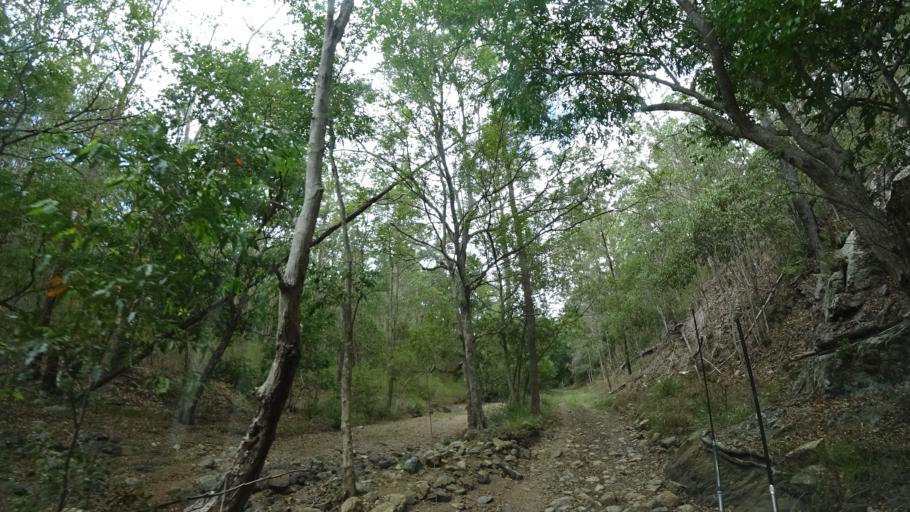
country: AU
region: Queensland
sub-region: Moreton Bay
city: Highvale
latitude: -27.4372
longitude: 152.7591
